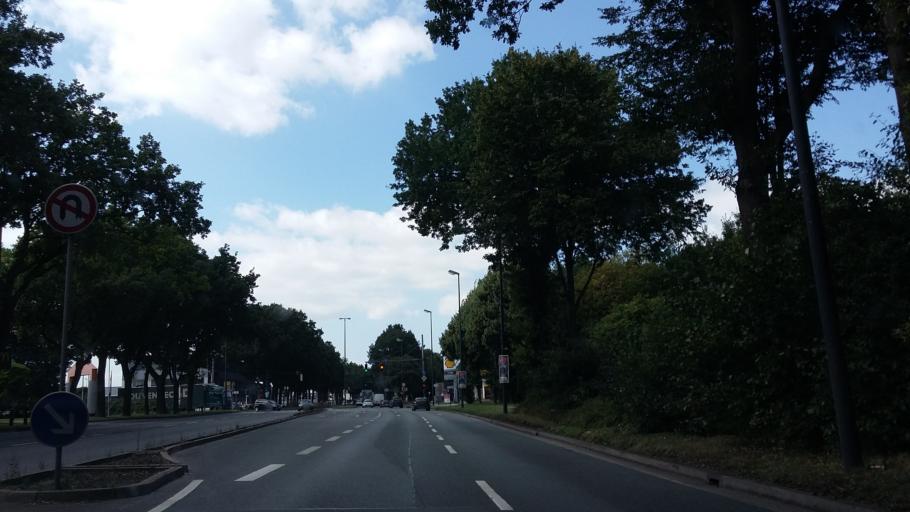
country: DE
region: Bremen
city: Bremen
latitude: 53.0543
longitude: 8.8012
